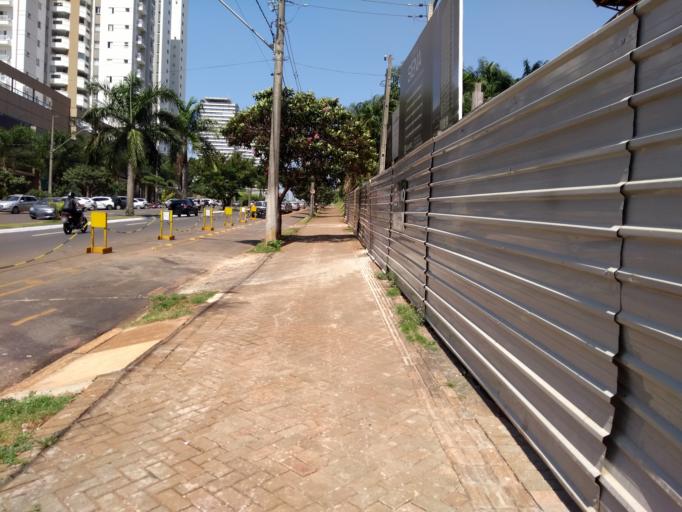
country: BR
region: Parana
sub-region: Londrina
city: Londrina
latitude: -23.3311
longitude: -51.1776
